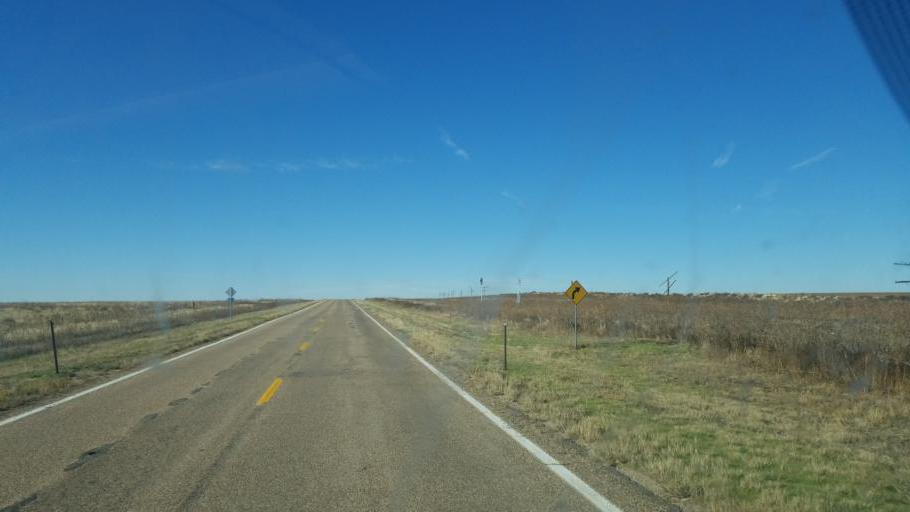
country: US
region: Colorado
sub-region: Otero County
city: La Junta
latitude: 38.2771
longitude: -103.4549
